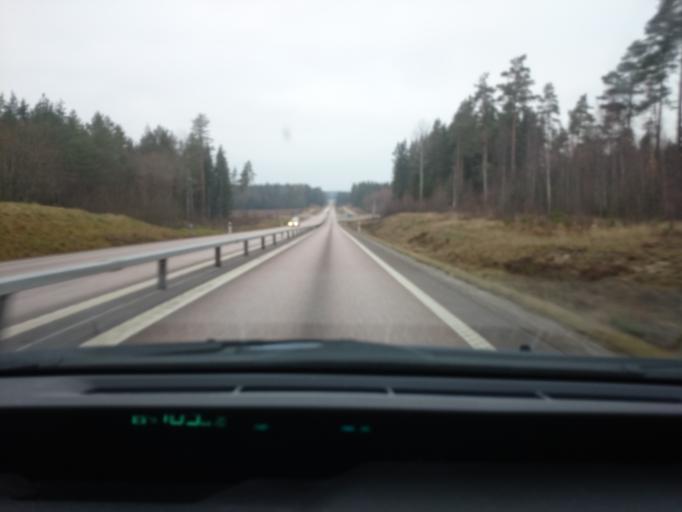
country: SE
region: Dalarna
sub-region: Avesta Kommun
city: Avesta
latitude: 60.0182
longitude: 16.3682
